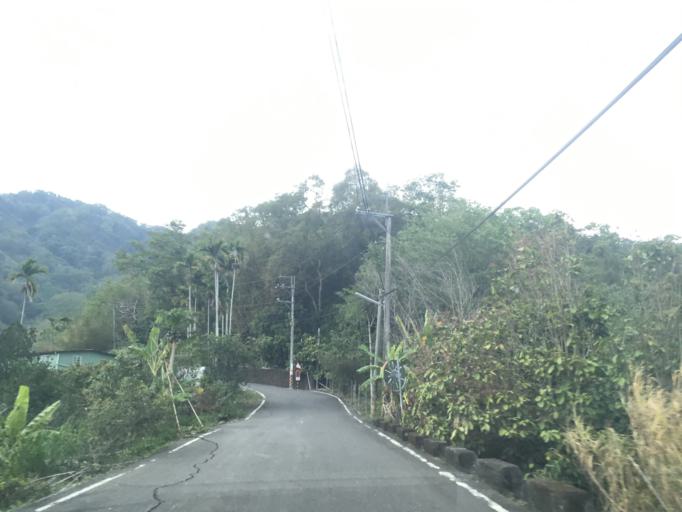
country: TW
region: Taiwan
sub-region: Nantou
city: Puli
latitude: 23.9528
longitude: 120.8652
